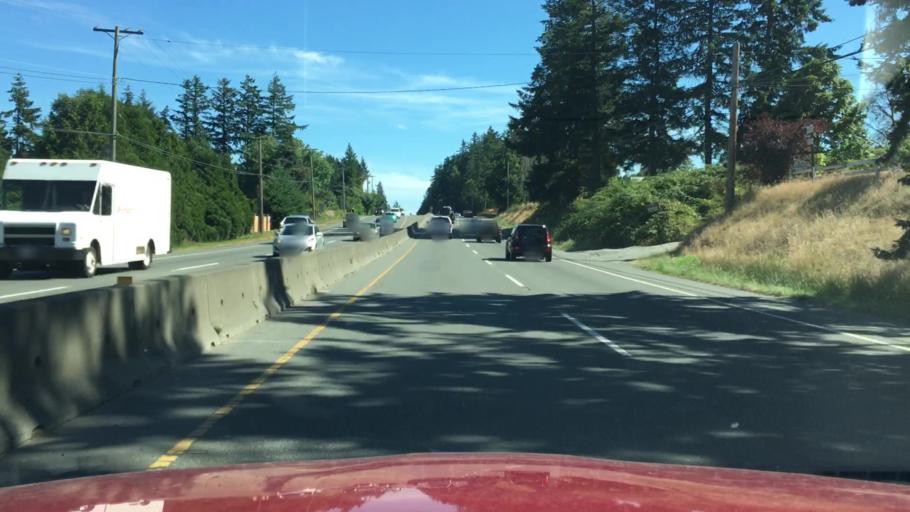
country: CA
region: British Columbia
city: Victoria
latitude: 48.5478
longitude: -123.3916
